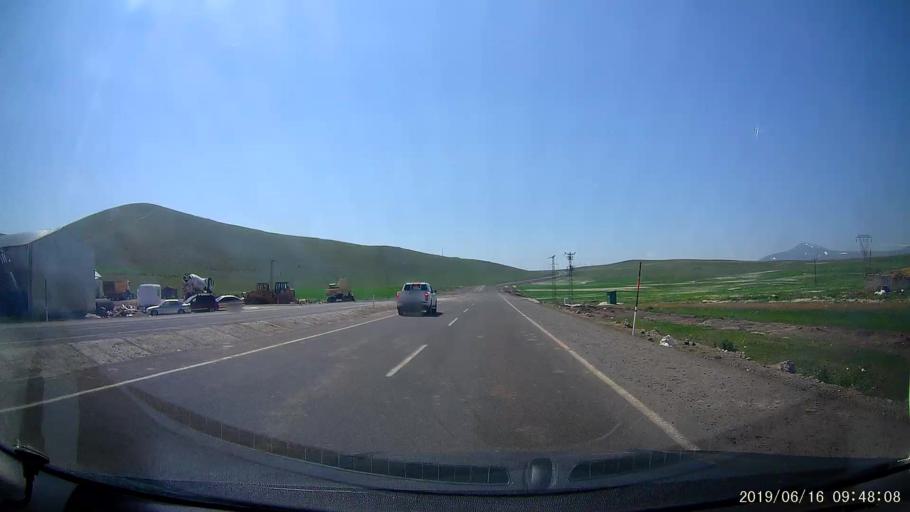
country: TR
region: Kars
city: Digor
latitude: 40.4368
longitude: 43.3511
